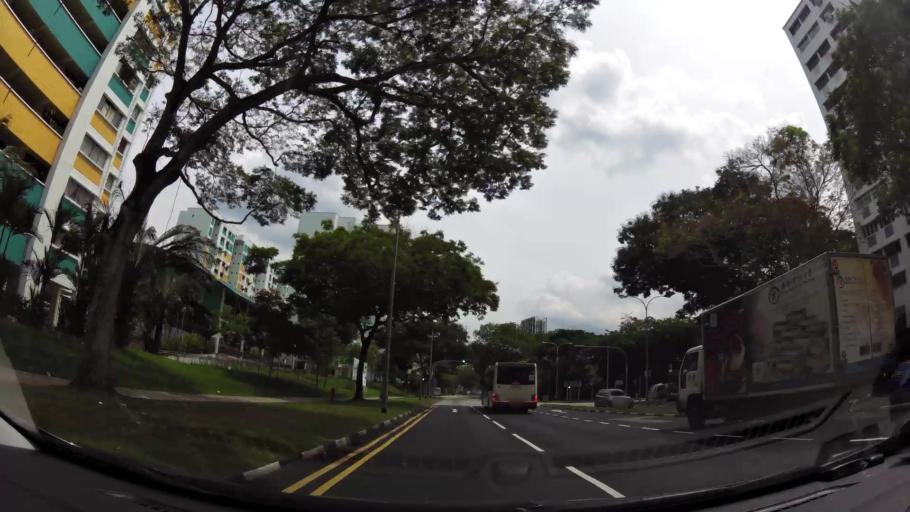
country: MY
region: Johor
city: Johor Bahru
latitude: 1.3746
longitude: 103.7715
